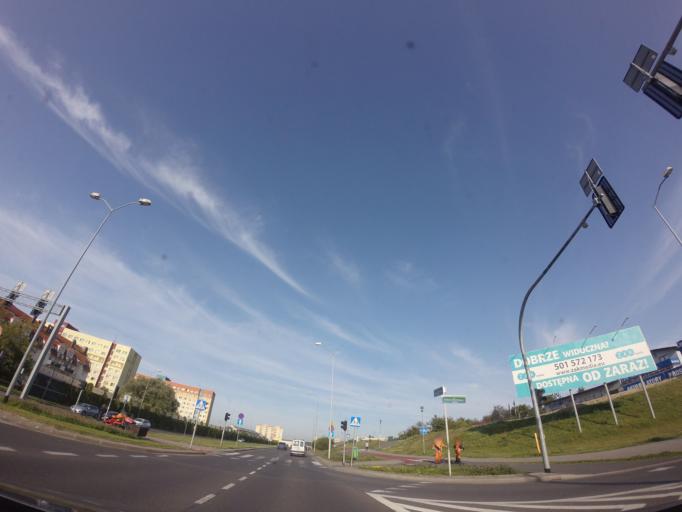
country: PL
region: West Pomeranian Voivodeship
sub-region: Szczecin
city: Szczecin
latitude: 53.4546
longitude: 14.5502
